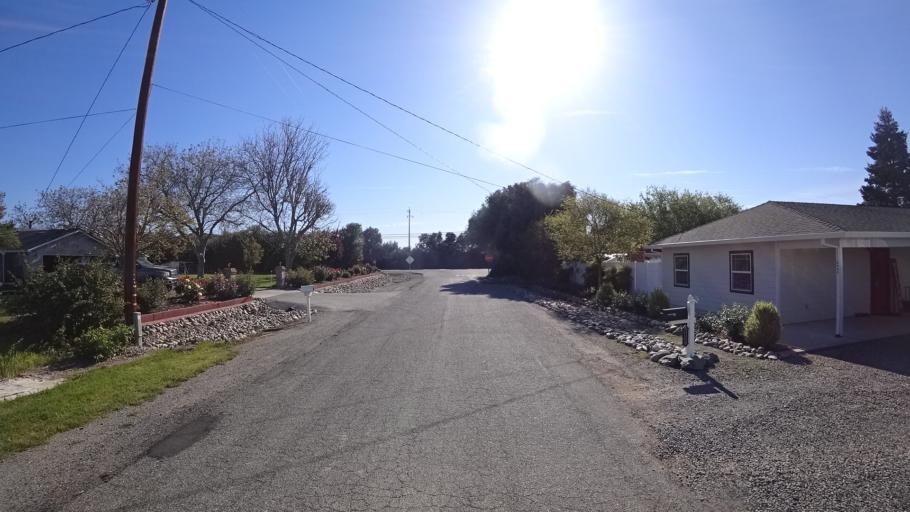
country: US
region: California
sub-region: Glenn County
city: Orland
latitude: 39.7149
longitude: -122.1978
